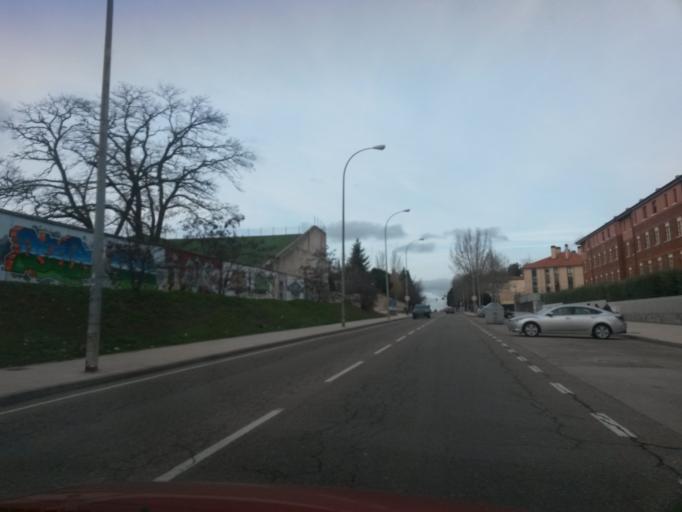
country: ES
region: Castille and Leon
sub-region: Provincia de Salamanca
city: Salamanca
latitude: 40.9803
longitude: -5.6611
